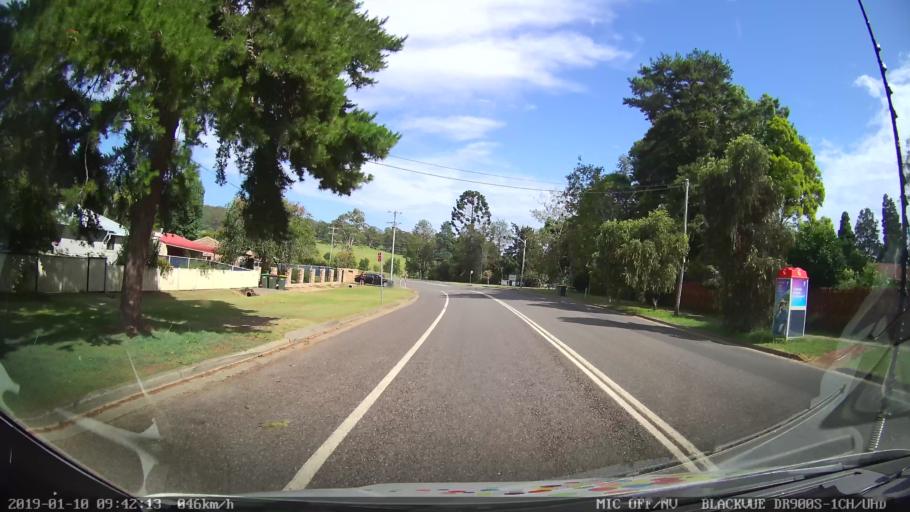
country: AU
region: New South Wales
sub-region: Coffs Harbour
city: Nana Glen
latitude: -30.1374
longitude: 153.0064
